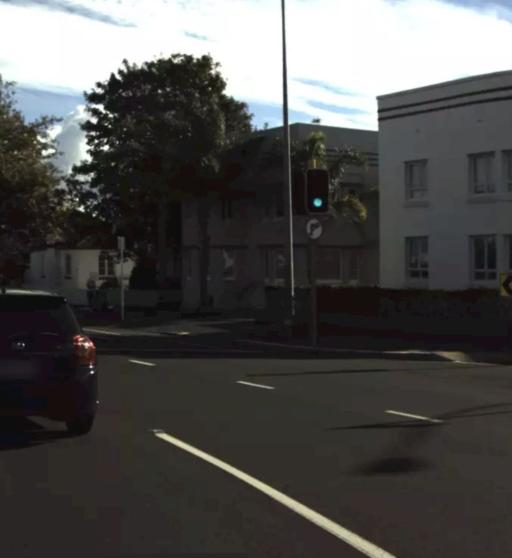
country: NZ
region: Auckland
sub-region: Auckland
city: Auckland
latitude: -36.8455
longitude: 174.7342
